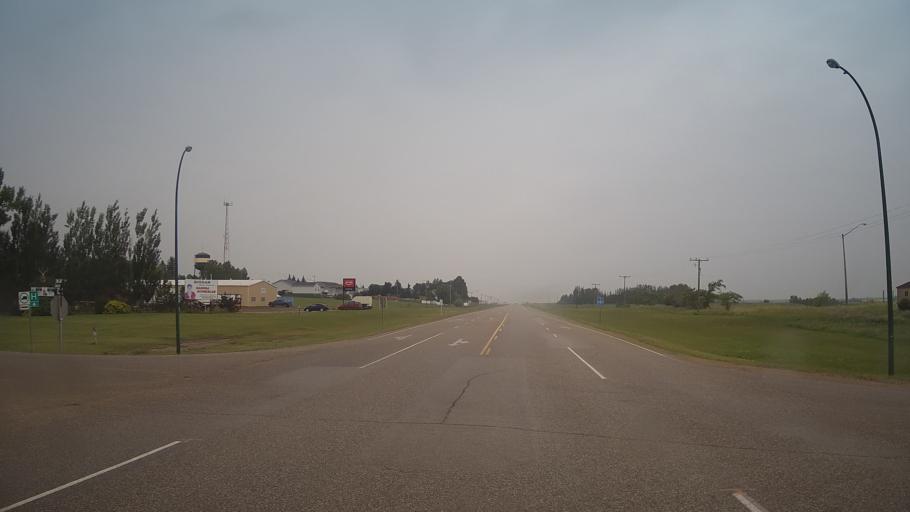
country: CA
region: Saskatchewan
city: Biggar
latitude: 52.0624
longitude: -107.9800
